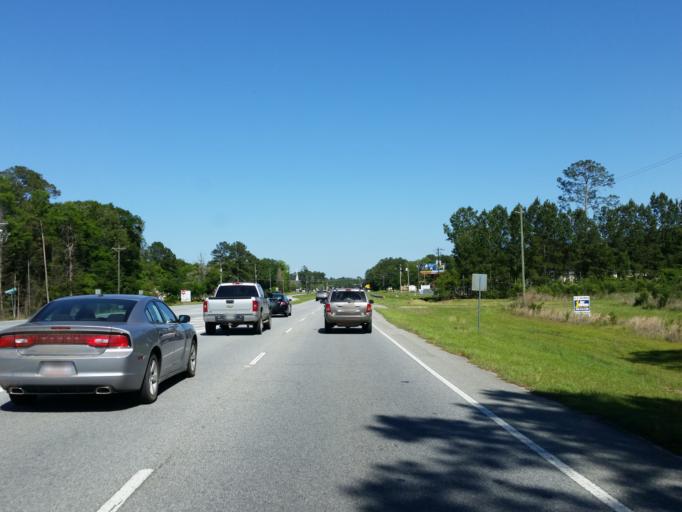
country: US
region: Georgia
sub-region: Lowndes County
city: Valdosta
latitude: 30.8826
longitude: -83.2572
